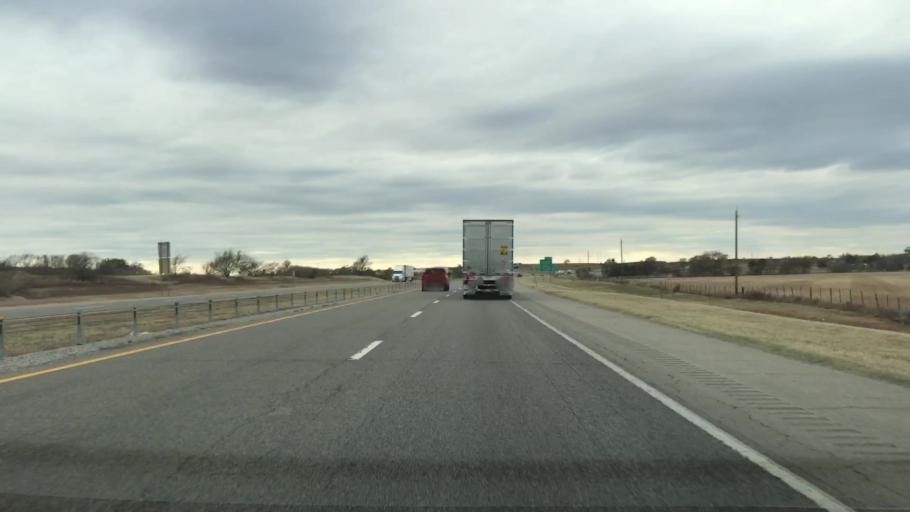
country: US
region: Oklahoma
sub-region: Washita County
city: Burns Flat
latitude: 35.4497
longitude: -99.1612
